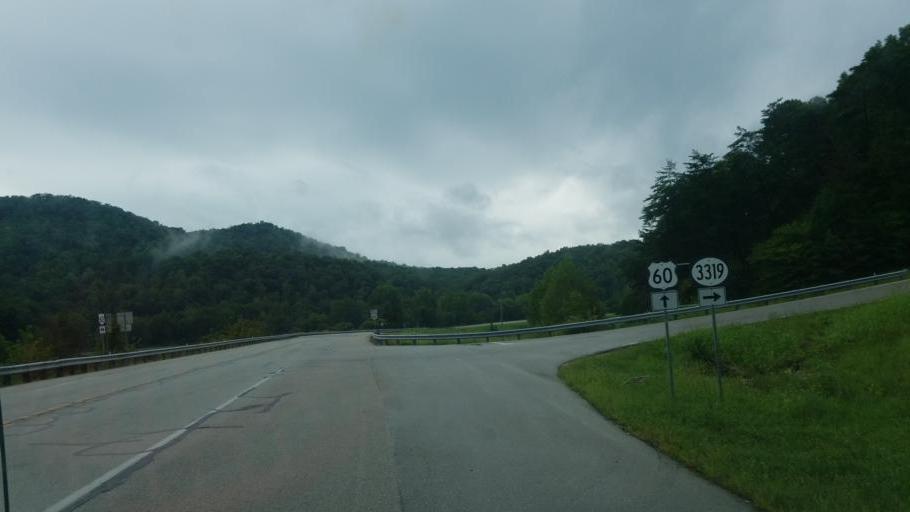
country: US
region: Kentucky
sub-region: Rowan County
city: Morehead
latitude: 38.1486
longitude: -83.5050
